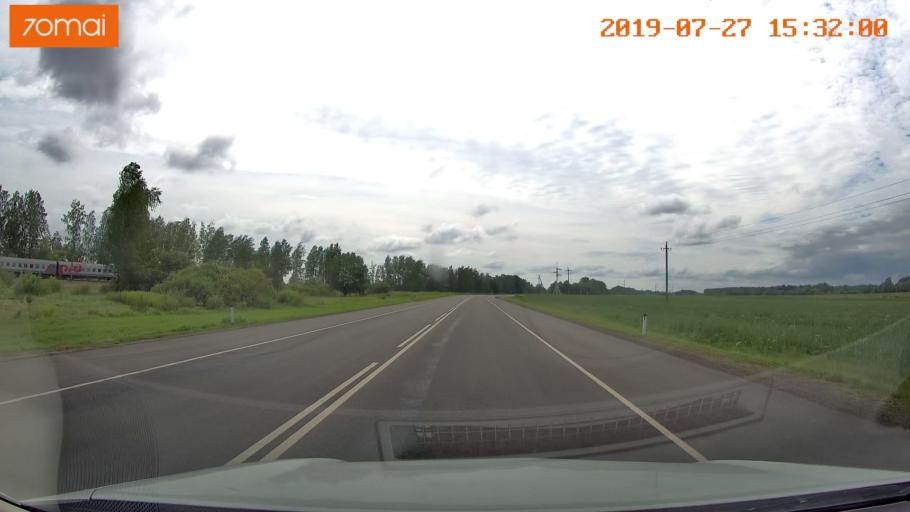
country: RU
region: Kaliningrad
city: Nesterov
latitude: 54.6183
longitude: 22.4806
